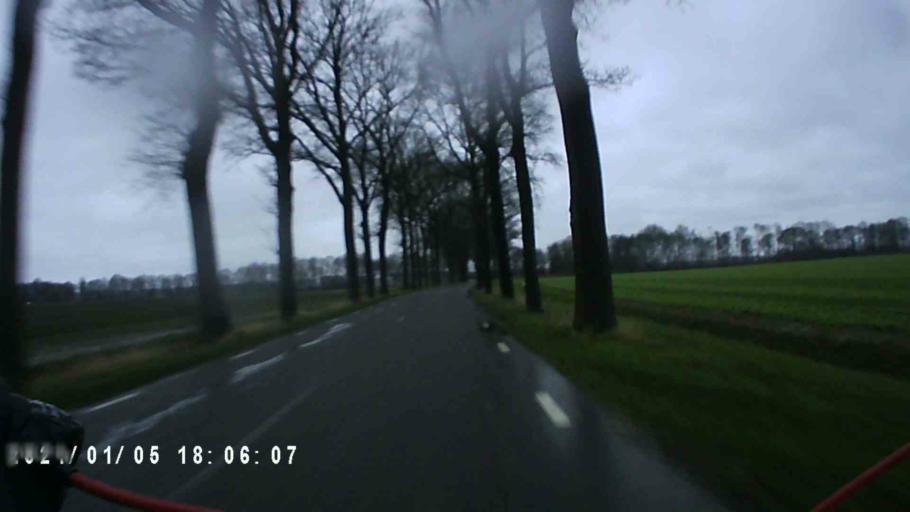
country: NL
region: Groningen
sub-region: Gemeente Slochteren
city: Slochteren
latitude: 53.1994
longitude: 6.8441
